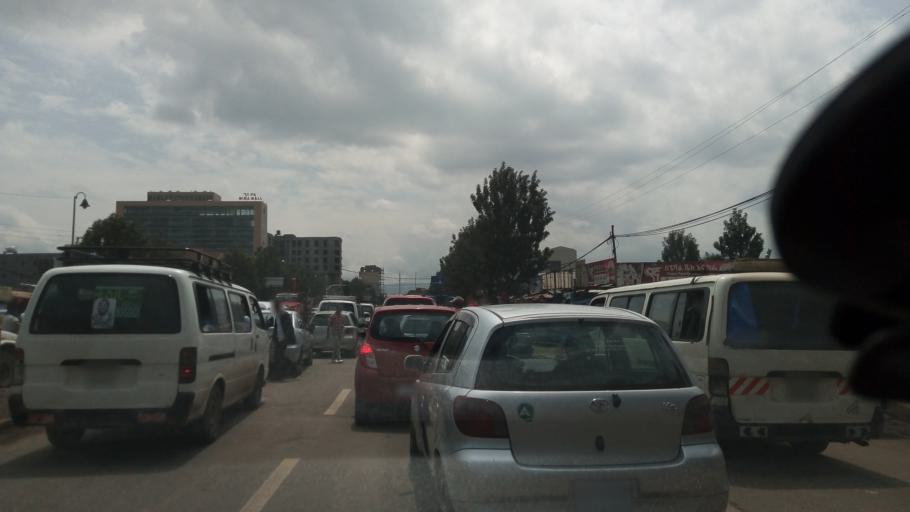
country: ET
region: Adis Abeba
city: Addis Ababa
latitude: 8.9671
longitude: 38.7209
